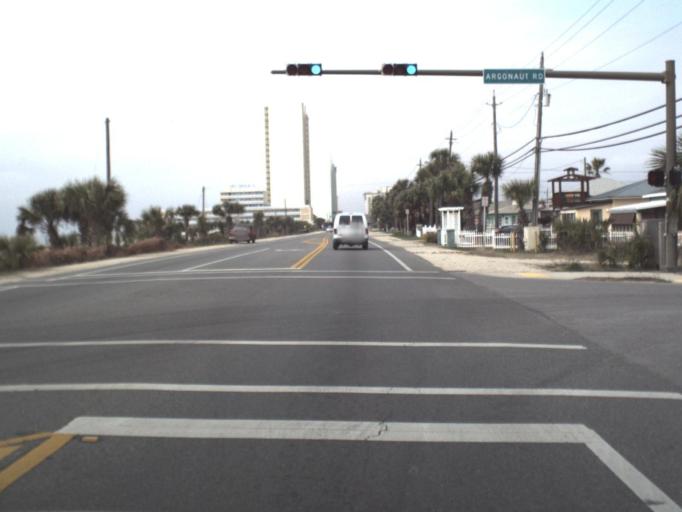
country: US
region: Florida
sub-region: Bay County
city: Panama City Beach
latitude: 30.2015
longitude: -85.8503
